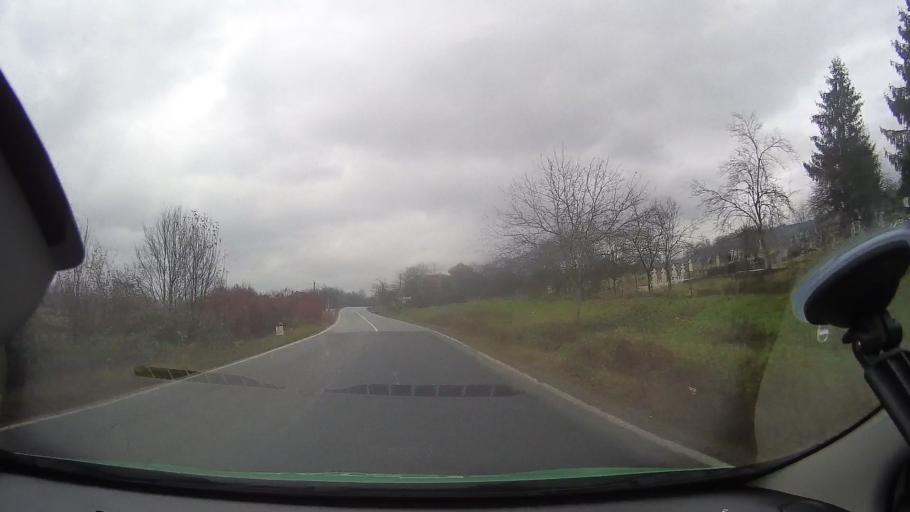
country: RO
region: Arad
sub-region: Comuna Buteni
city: Buteni
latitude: 46.2994
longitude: 22.1702
